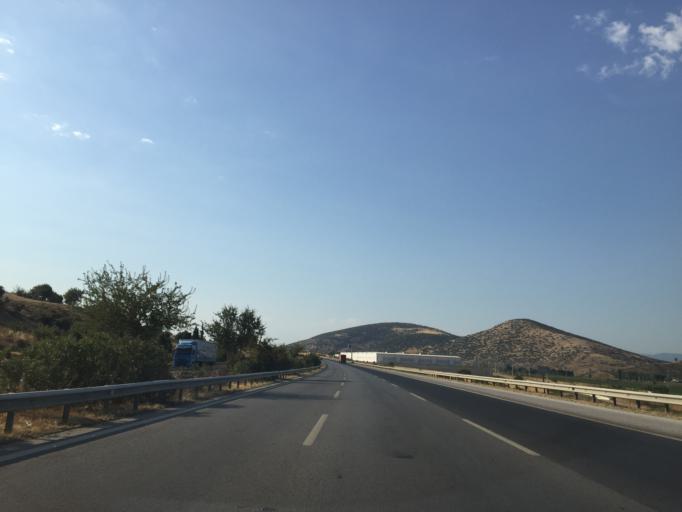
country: TR
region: Izmir
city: Belevi
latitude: 38.0473
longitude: 27.4283
